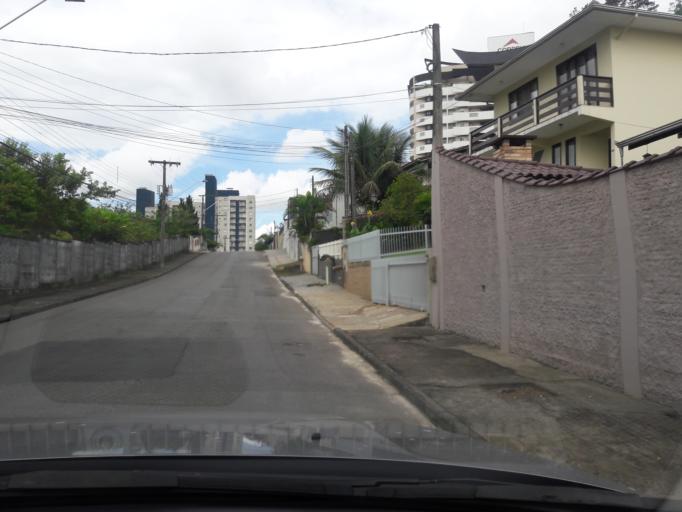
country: BR
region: Santa Catarina
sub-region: Joinville
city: Joinville
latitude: -26.3205
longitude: -48.8639
